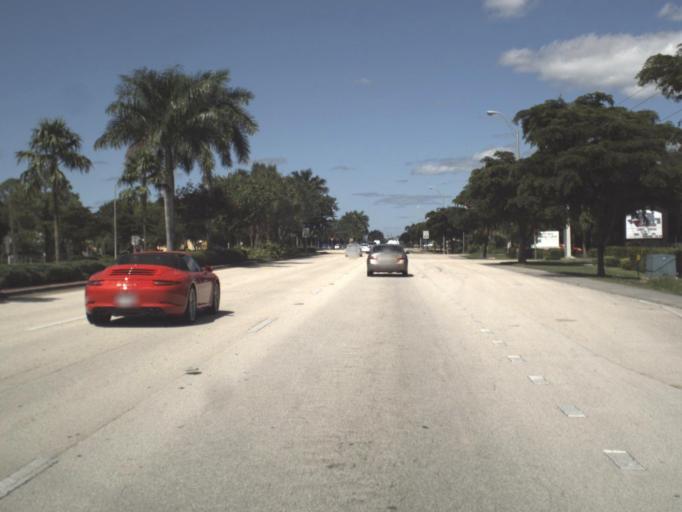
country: US
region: Florida
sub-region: Collier County
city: Lely
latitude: 26.1117
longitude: -81.7518
